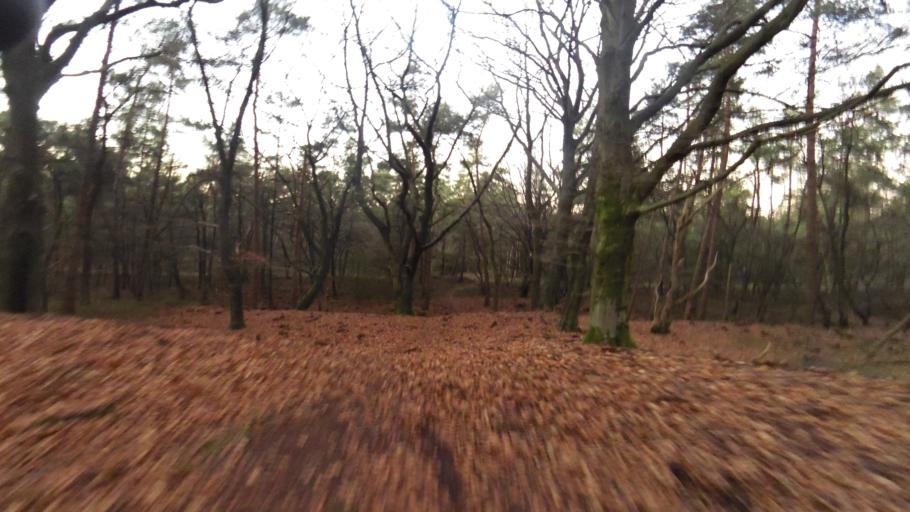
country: NL
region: Gelderland
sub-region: Gemeente Apeldoorn
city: Uddel
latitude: 52.2174
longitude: 5.8195
